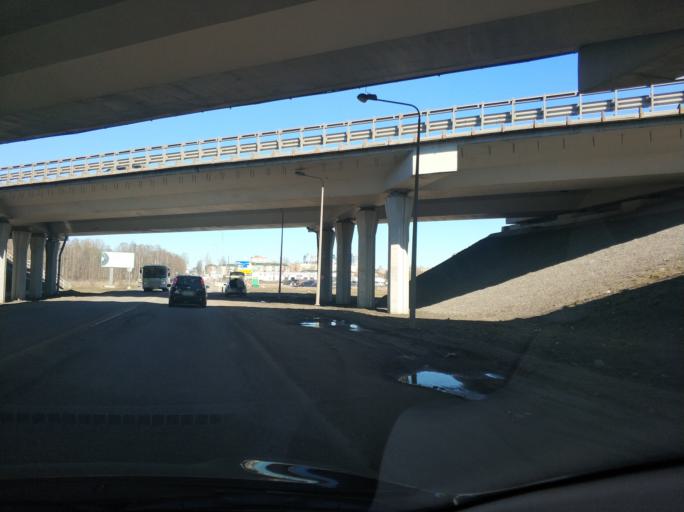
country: RU
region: Leningrad
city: Bugry
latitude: 60.0620
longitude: 30.3869
